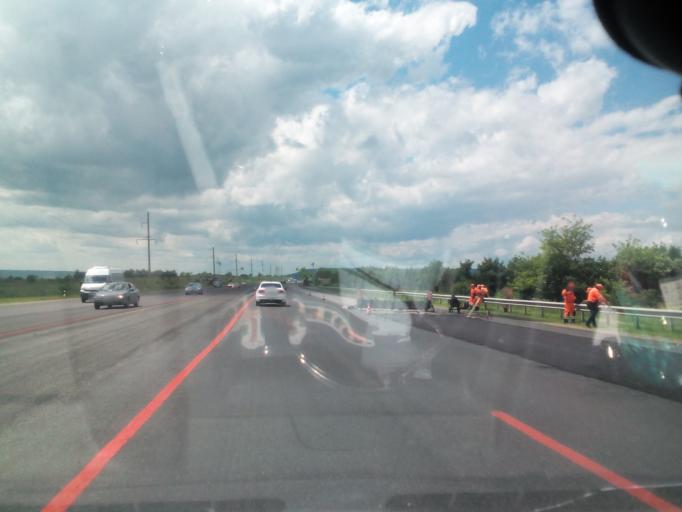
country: RU
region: Stavropol'skiy
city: Tatarka
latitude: 44.9516
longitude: 41.9573
